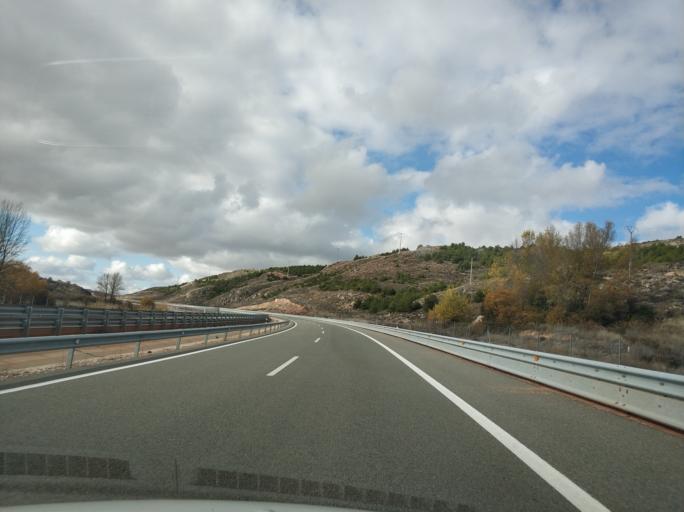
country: ES
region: Castille and Leon
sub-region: Provincia de Soria
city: Medinaceli
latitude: 41.1926
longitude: -2.4346
